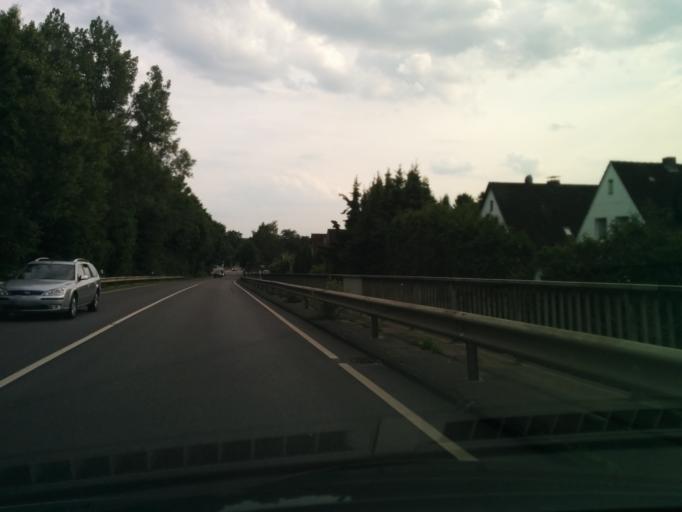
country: DE
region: Lower Saxony
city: Seevetal
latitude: 53.4076
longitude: 9.9803
